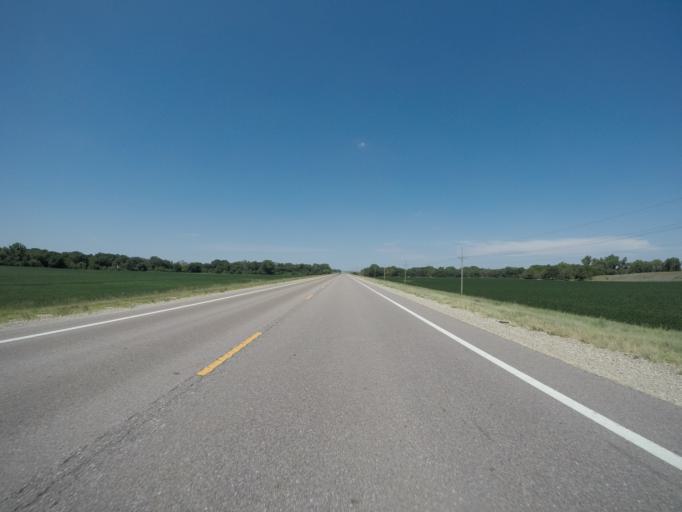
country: US
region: Kansas
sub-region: Osborne County
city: Osborne
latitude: 39.5096
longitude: -98.5919
